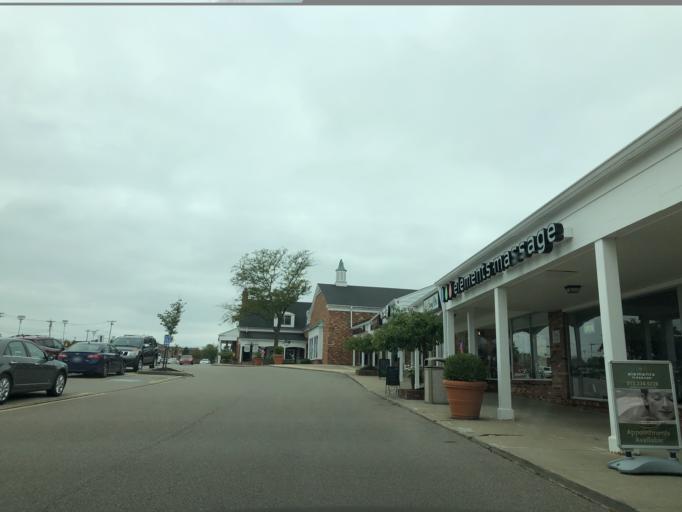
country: US
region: Ohio
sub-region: Hamilton County
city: Montgomery
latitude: 39.2373
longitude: -84.3509
